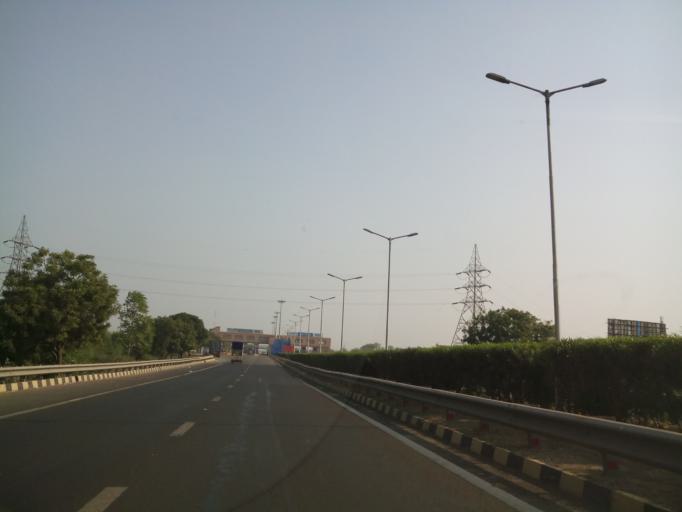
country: IN
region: Gujarat
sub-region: Ahmadabad
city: Ahmedabad
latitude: 22.9774
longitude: 72.6476
